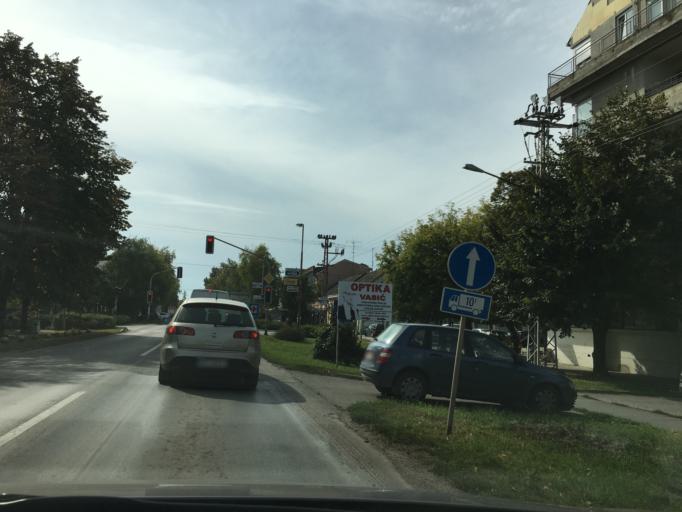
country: RS
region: Autonomna Pokrajina Vojvodina
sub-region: Juznobacki Okrug
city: Temerin
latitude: 45.4100
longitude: 19.8888
